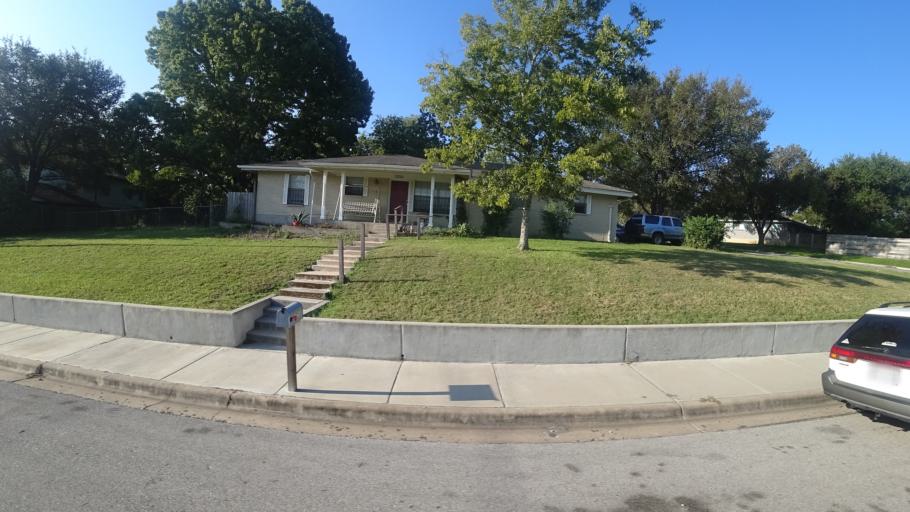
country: US
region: Texas
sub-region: Travis County
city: Austin
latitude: 30.3099
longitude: -97.6724
